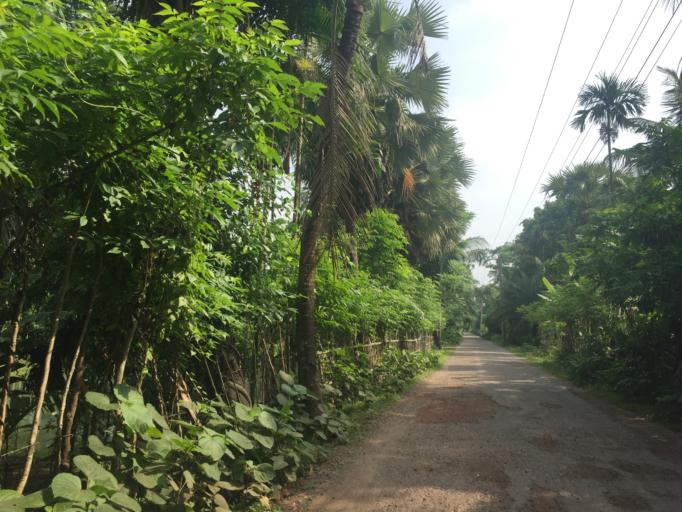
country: BD
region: Barisal
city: Mathba
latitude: 22.2208
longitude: 89.9161
